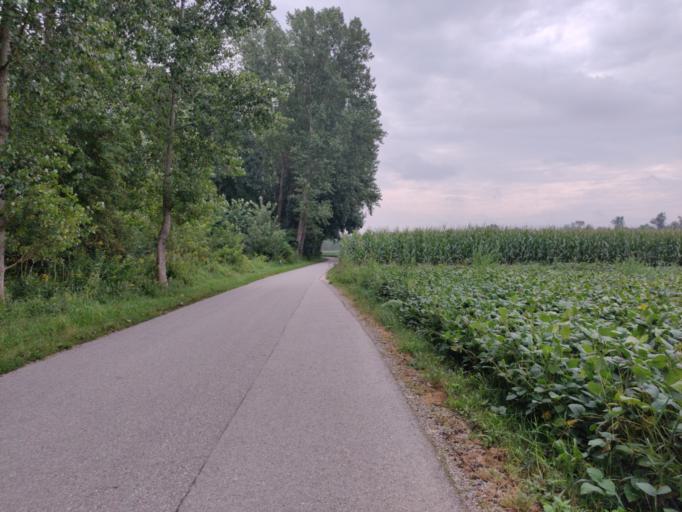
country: AT
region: Upper Austria
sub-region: Politischer Bezirk Linz-Land
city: Enns
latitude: 48.2341
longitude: 14.4691
